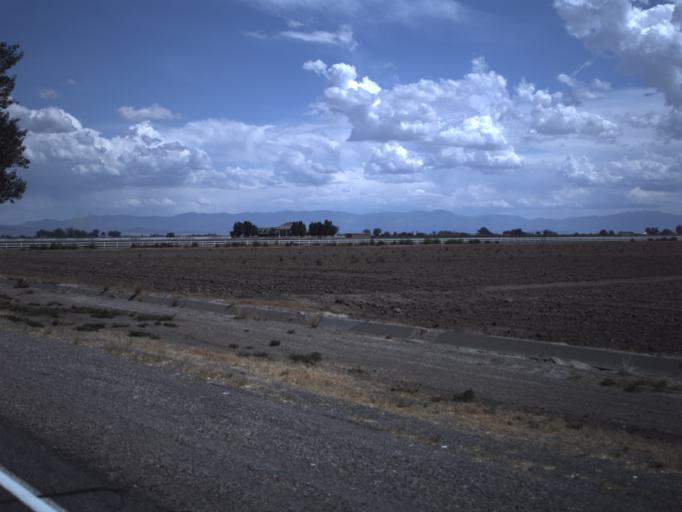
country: US
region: Utah
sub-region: Millard County
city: Delta
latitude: 39.3306
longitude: -112.6398
